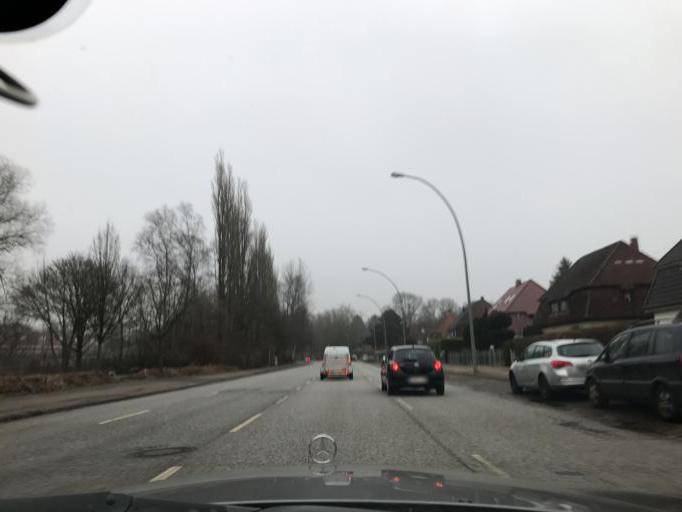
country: DE
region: Hamburg
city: Farmsen-Berne
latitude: 53.6103
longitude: 10.1227
